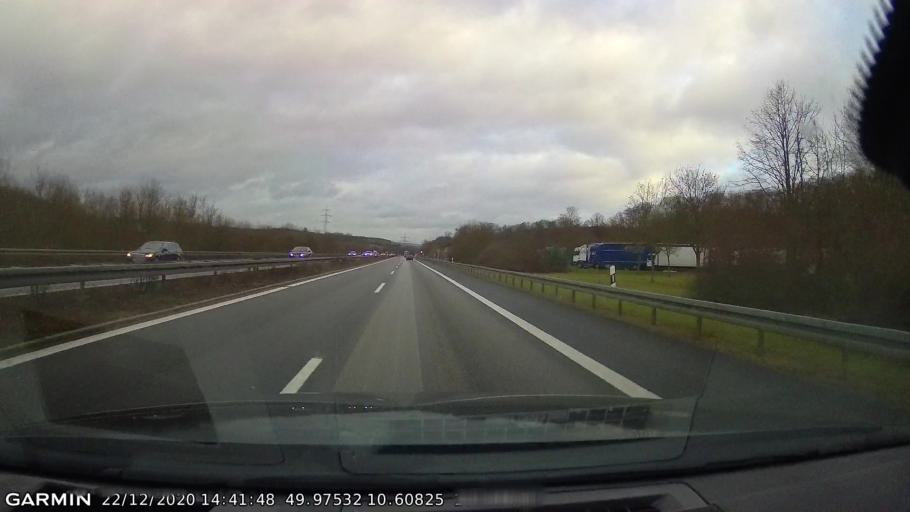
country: DE
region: Bavaria
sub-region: Regierungsbezirk Unterfranken
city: Sand
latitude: 49.9750
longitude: 10.6075
